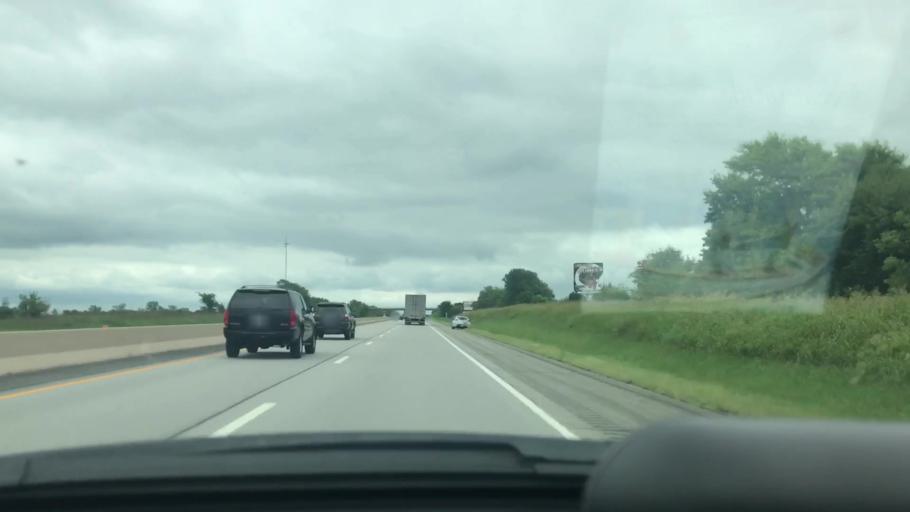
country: US
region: Oklahoma
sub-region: Ottawa County
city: Commerce
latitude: 36.9080
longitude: -94.7934
